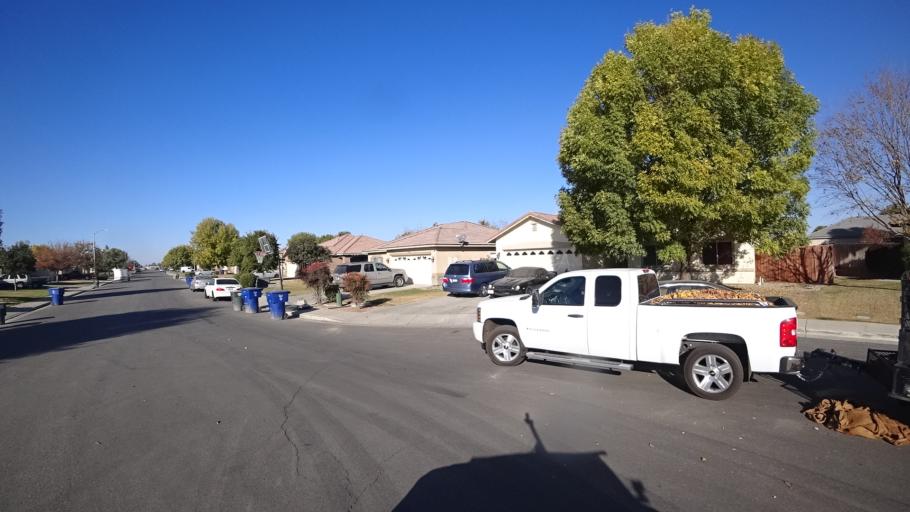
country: US
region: California
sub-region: Kern County
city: Greenfield
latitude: 35.2692
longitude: -119.0397
